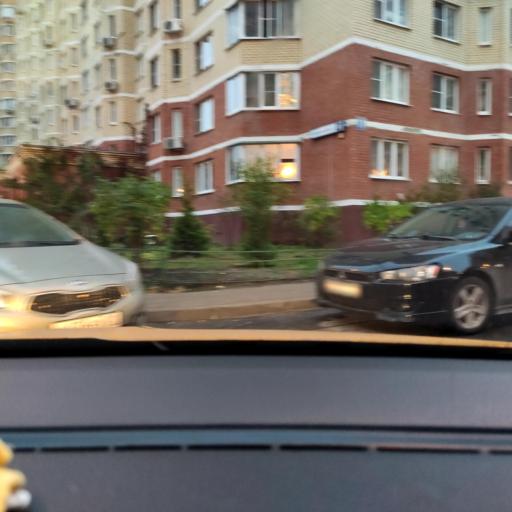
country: RU
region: Moskovskaya
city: Moskovskiy
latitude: 55.5946
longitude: 37.3423
